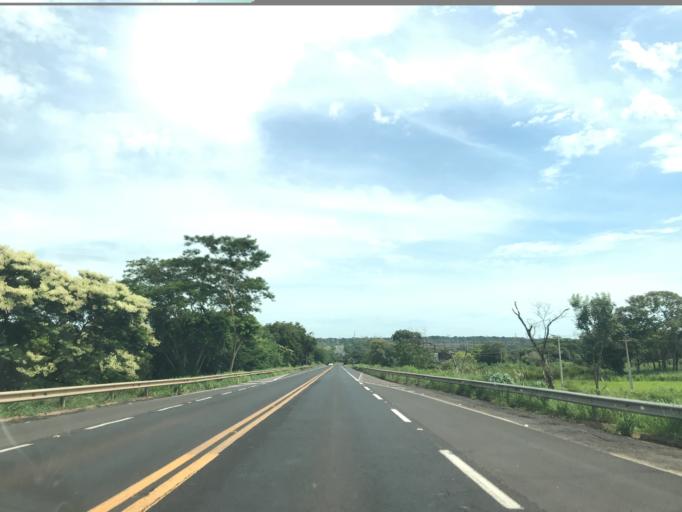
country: BR
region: Sao Paulo
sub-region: Nova Granada
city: Nova Granada
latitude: -20.3166
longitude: -49.2099
